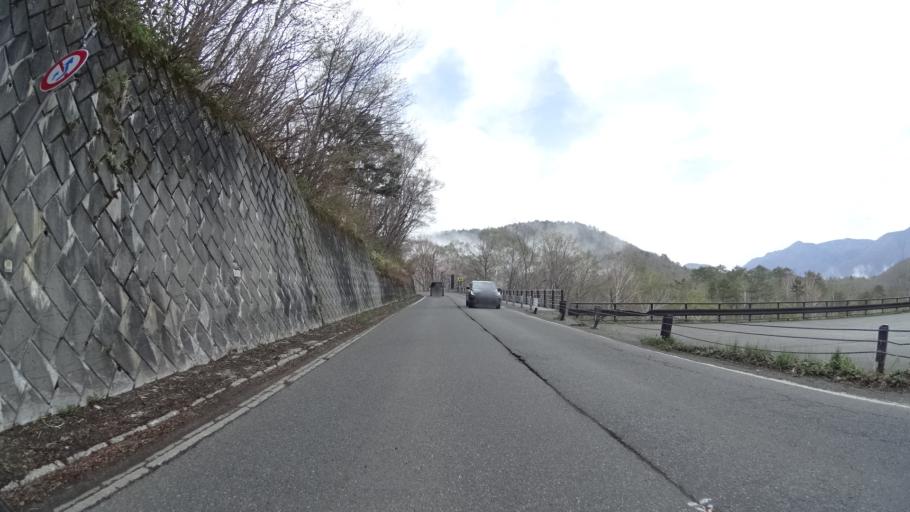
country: JP
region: Nagano
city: Nakano
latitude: 36.7177
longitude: 138.4822
